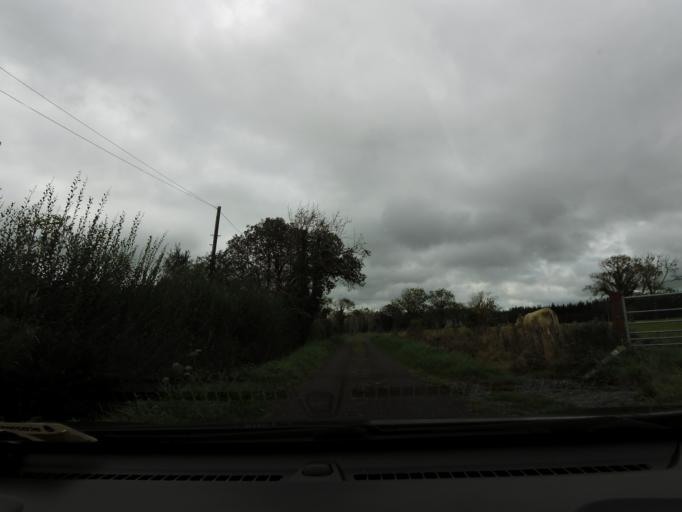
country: IE
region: Connaught
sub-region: County Galway
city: Athenry
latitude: 53.2977
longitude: -8.6674
